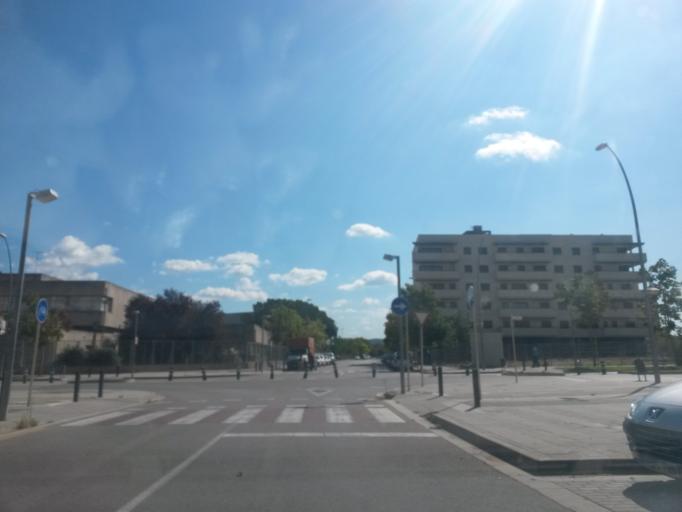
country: ES
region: Catalonia
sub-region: Provincia de Girona
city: Salt
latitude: 41.9726
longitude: 2.8004
